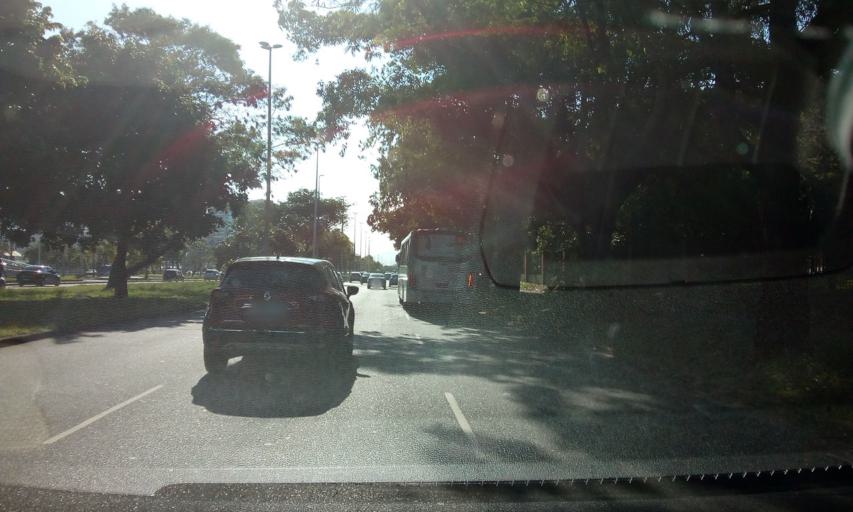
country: BR
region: Rio de Janeiro
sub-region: Nilopolis
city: Nilopolis
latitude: -23.0001
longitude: -43.3828
